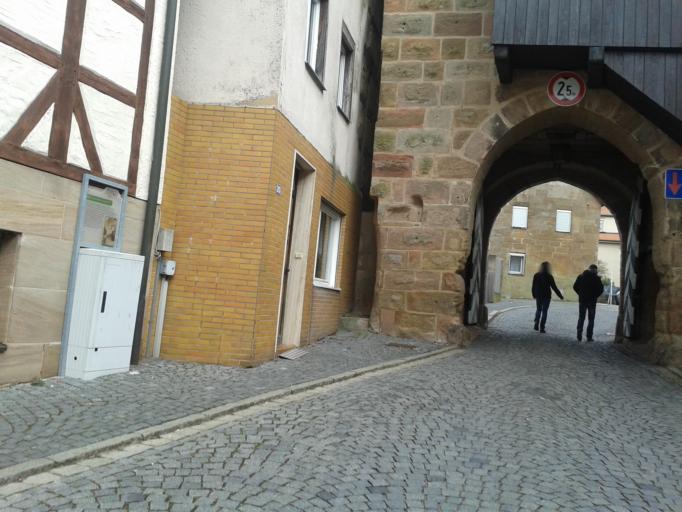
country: DE
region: Bavaria
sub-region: Regierungsbezirk Mittelfranken
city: Cadolzburg
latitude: 49.4577
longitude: 10.8525
